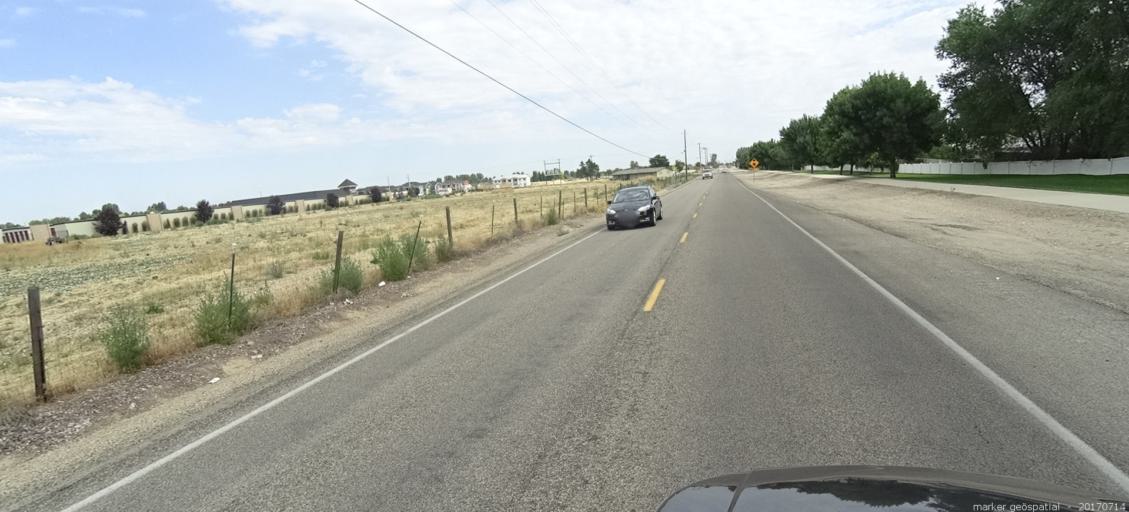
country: US
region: Idaho
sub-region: Ada County
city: Kuna
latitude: 43.5006
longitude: -116.4337
